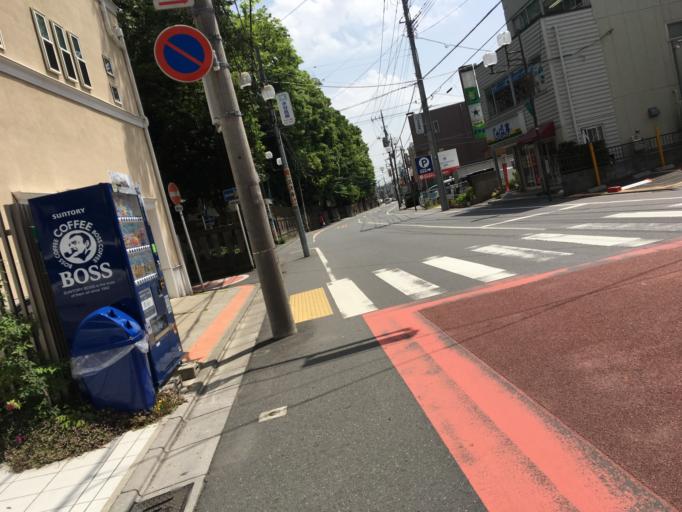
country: JP
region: Saitama
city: Yono
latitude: 35.8542
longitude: 139.6549
